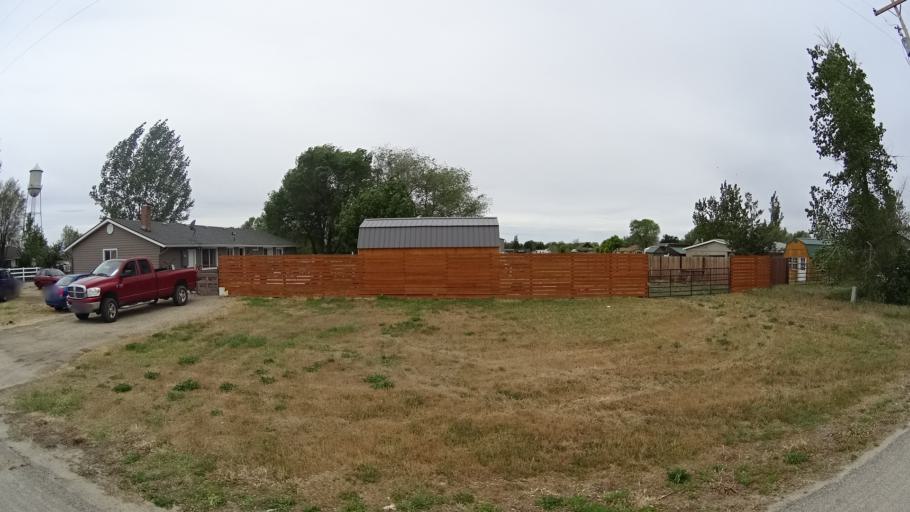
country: US
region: Idaho
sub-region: Ada County
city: Kuna
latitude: 43.4824
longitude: -116.3143
